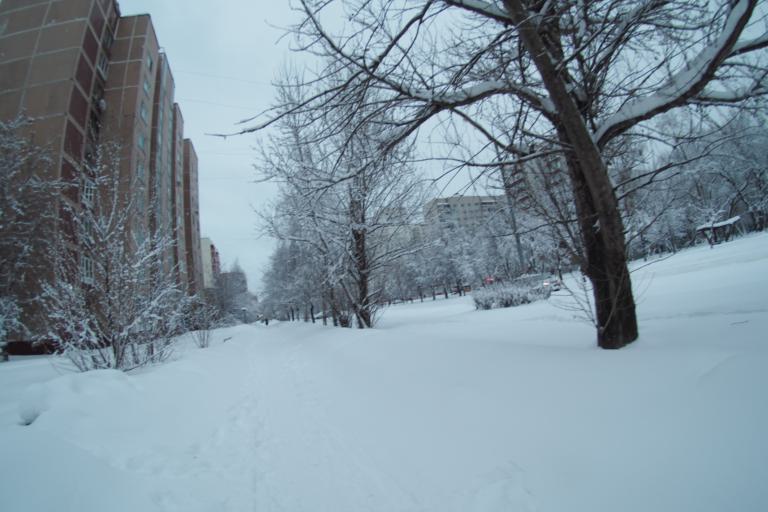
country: RU
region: Moscow
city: Ryazanskiy
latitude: 55.7400
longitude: 37.7686
